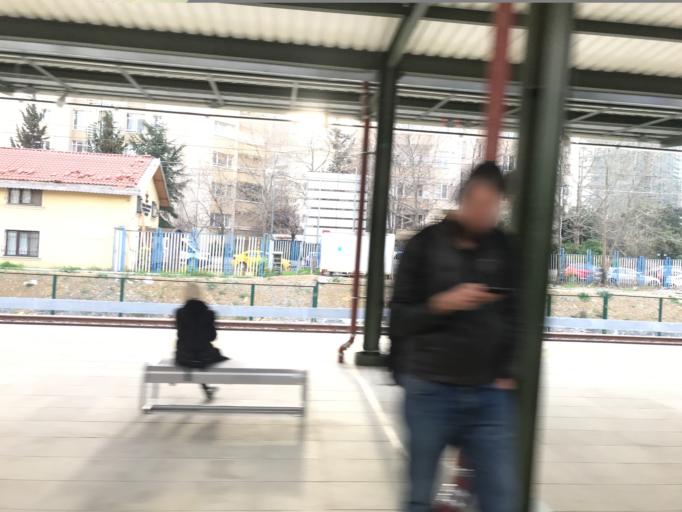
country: TR
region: Istanbul
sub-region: Atasehir
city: Atasehir
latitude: 40.9709
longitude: 29.0766
